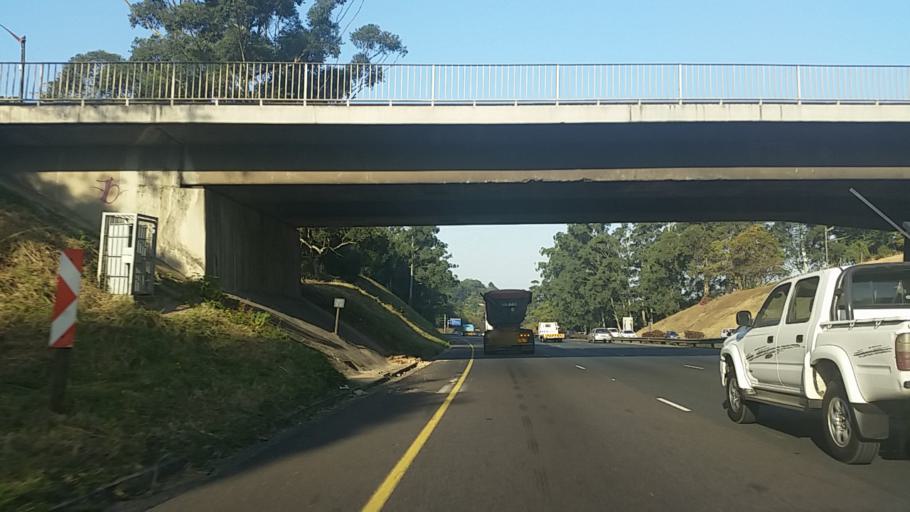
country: ZA
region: KwaZulu-Natal
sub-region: eThekwini Metropolitan Municipality
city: Berea
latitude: -29.8404
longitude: 30.9142
